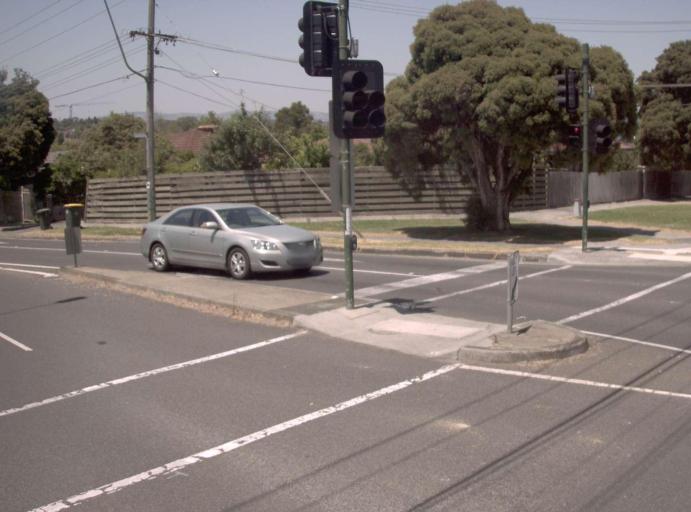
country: AU
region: Victoria
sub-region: Whitehorse
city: Forest Hill
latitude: -37.8484
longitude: 145.1706
